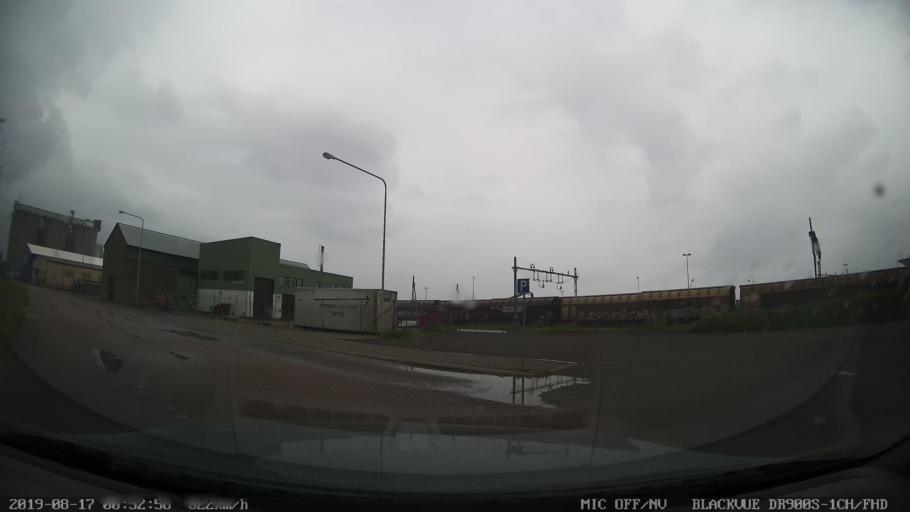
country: SE
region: Skane
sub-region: Landskrona
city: Landskrona
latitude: 55.8651
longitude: 12.8293
